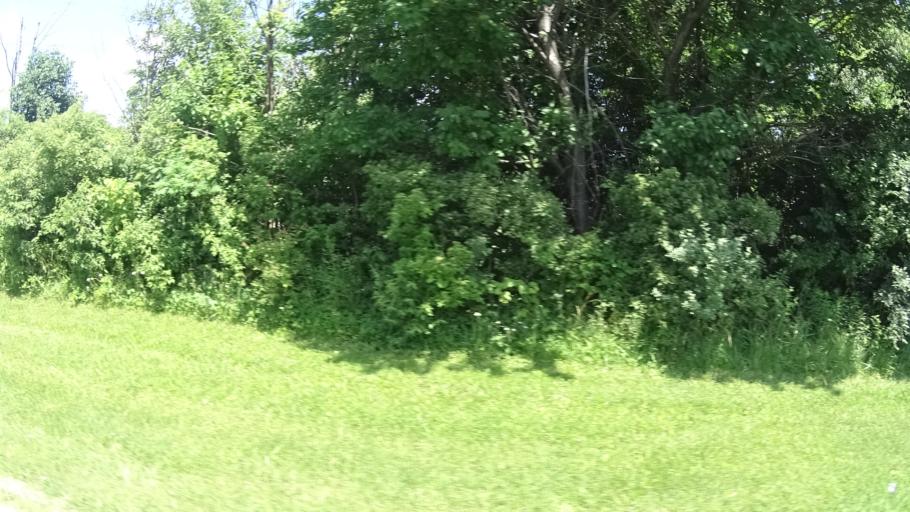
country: US
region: Ohio
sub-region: Lorain County
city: Vermilion
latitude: 41.3414
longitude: -82.3795
